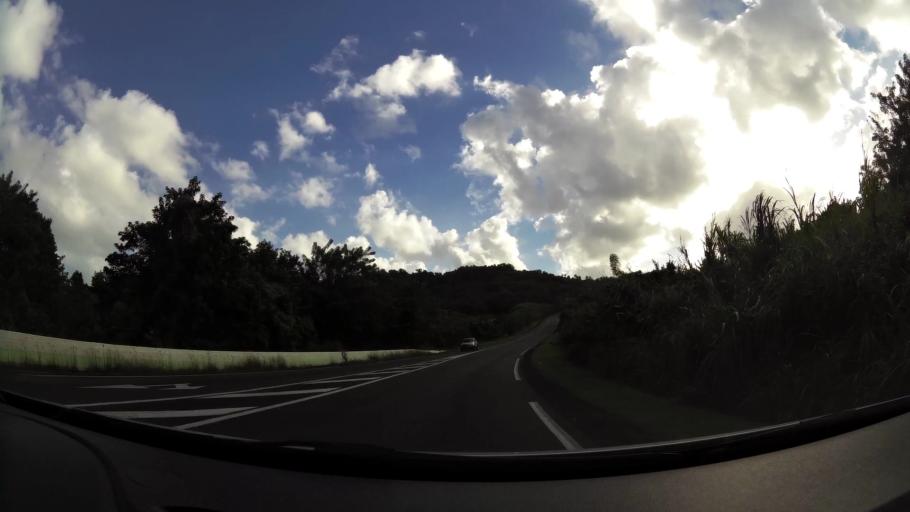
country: MQ
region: Martinique
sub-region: Martinique
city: Ducos
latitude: 14.6031
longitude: -60.9625
